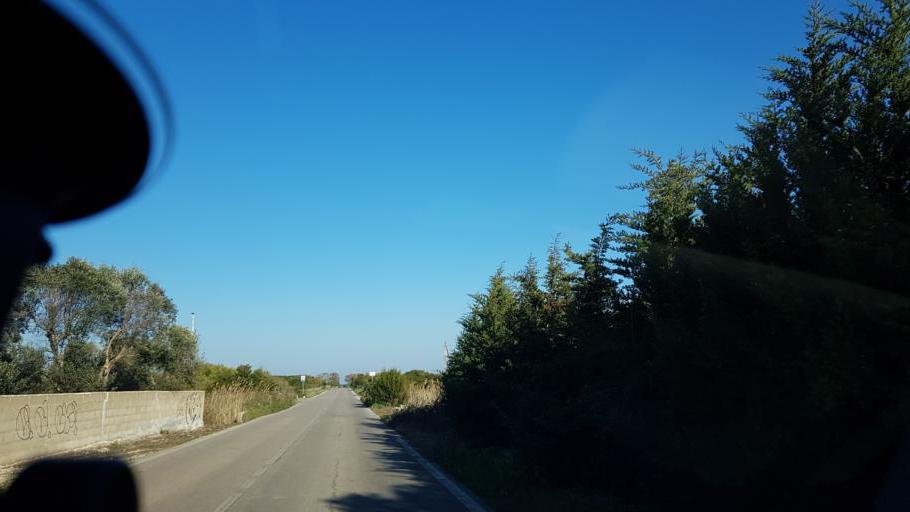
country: IT
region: Apulia
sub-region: Provincia di Lecce
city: Giorgilorio
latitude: 40.4563
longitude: 18.2043
